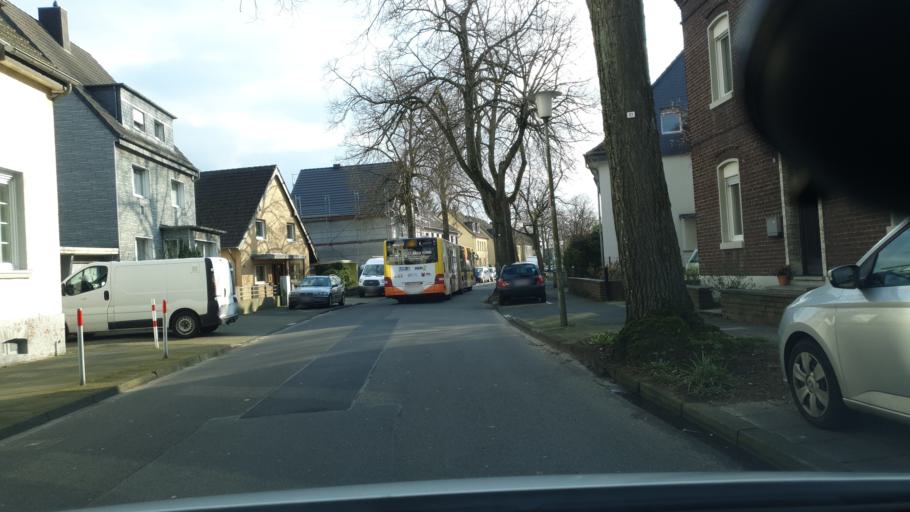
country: DE
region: North Rhine-Westphalia
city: Opladen
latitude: 51.0430
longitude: 7.0501
